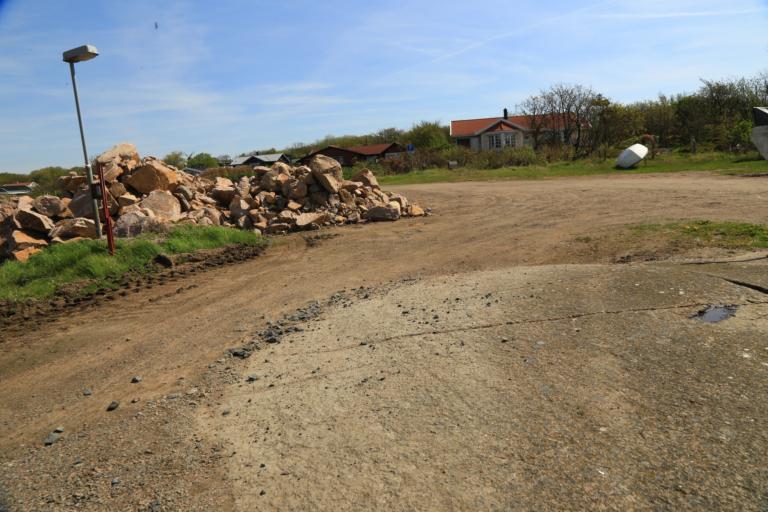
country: SE
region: Halland
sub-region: Varbergs Kommun
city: Varberg
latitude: 57.1375
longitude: 12.2192
